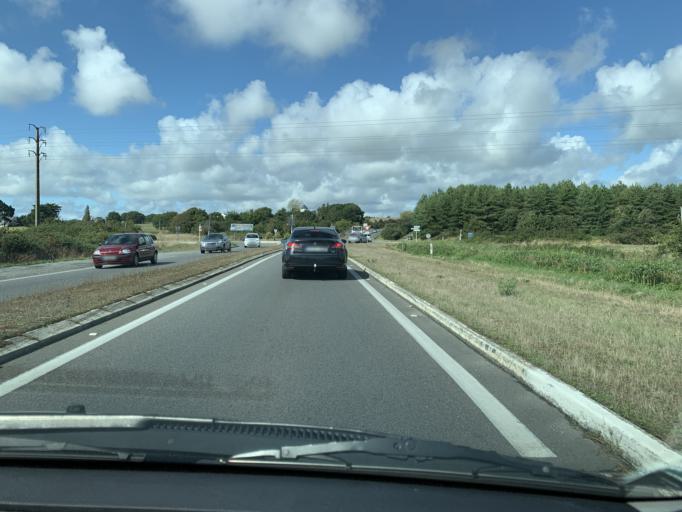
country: FR
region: Pays de la Loire
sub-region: Departement de la Loire-Atlantique
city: Guerande
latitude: 47.3140
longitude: -2.4288
